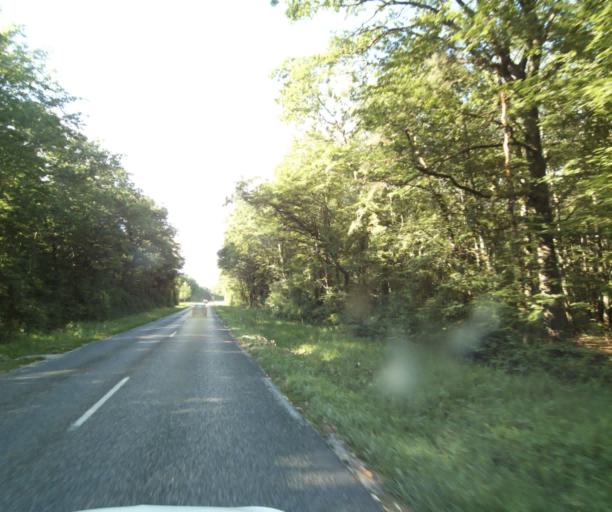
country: FR
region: Rhone-Alpes
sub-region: Departement de la Haute-Savoie
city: Messery
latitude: 46.3337
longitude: 6.2920
